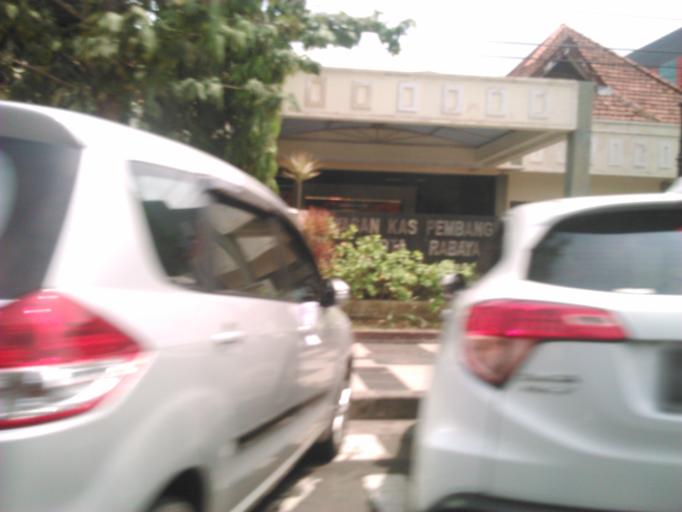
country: ID
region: East Java
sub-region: Kota Surabaya
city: Surabaya
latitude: -7.2584
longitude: 112.7480
